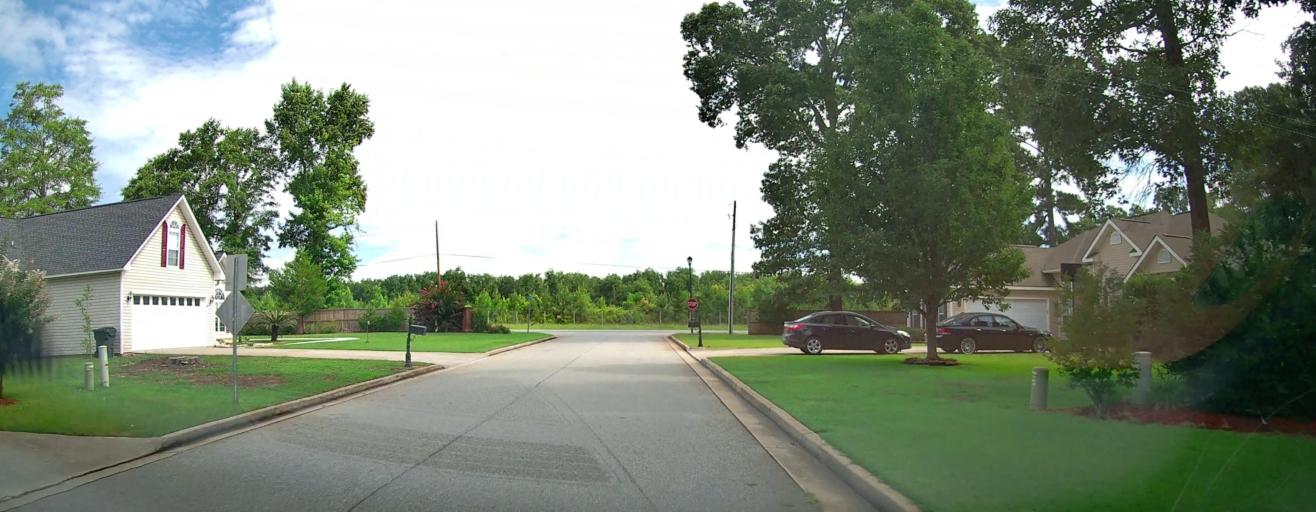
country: US
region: Georgia
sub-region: Peach County
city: Byron
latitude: 32.6507
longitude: -83.7245
